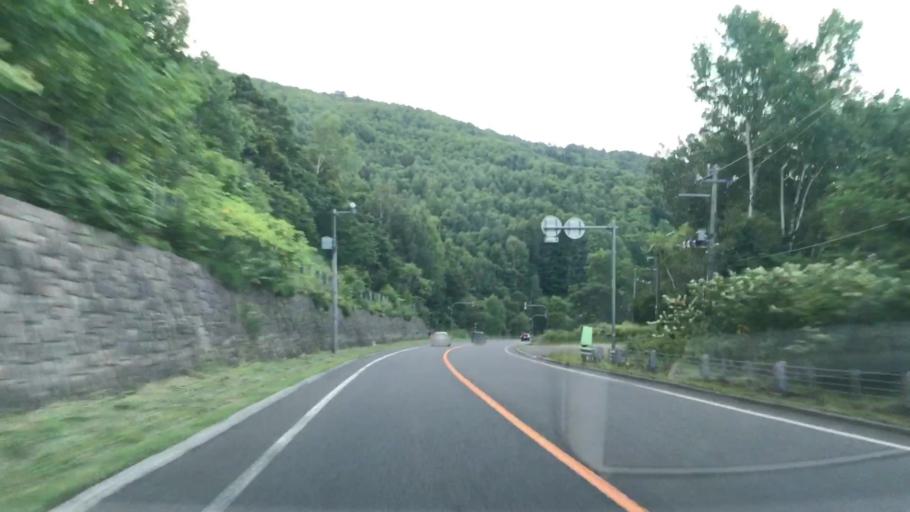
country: JP
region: Hokkaido
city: Sapporo
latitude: 42.9090
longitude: 141.1203
